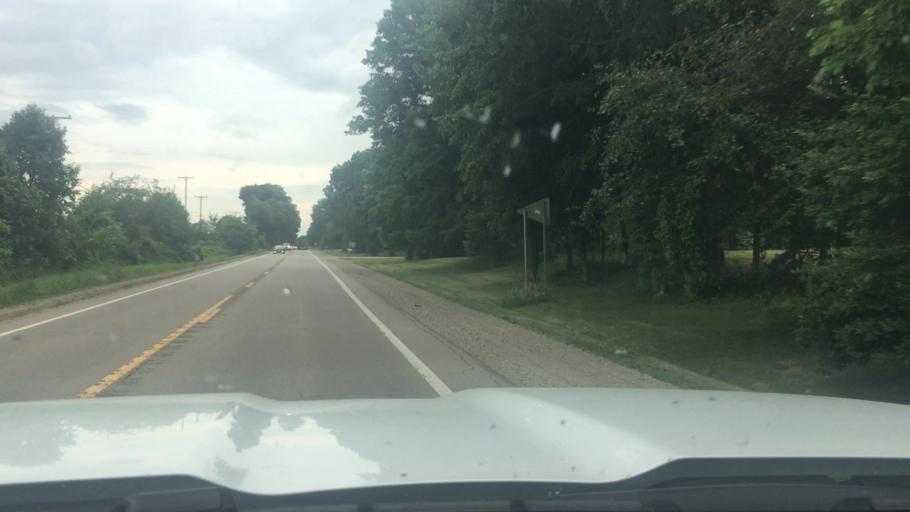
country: US
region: Michigan
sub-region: Ionia County
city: Ionia
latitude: 43.0019
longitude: -85.0023
